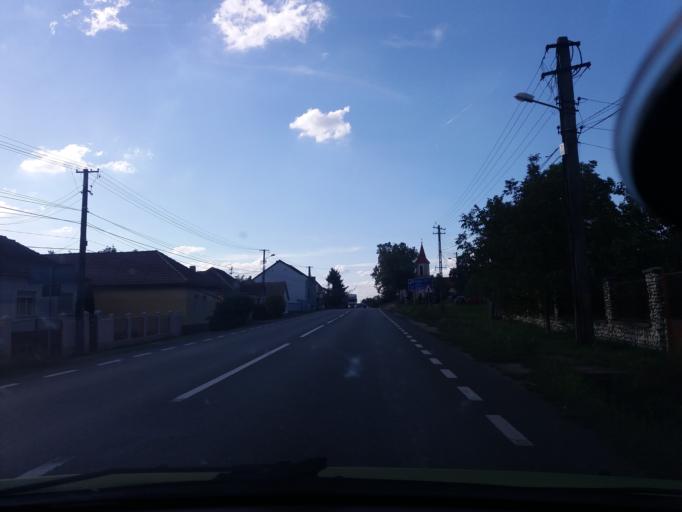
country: RO
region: Arad
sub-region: Comuna Paulis
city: Paulis
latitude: 46.1104
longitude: 21.5995
